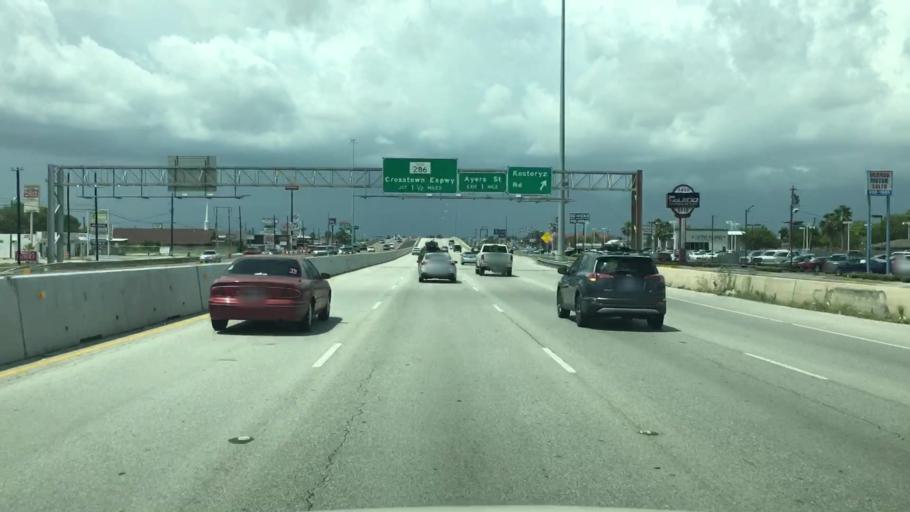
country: US
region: Texas
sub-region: Nueces County
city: Corpus Christi
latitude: 27.7264
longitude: -97.4083
